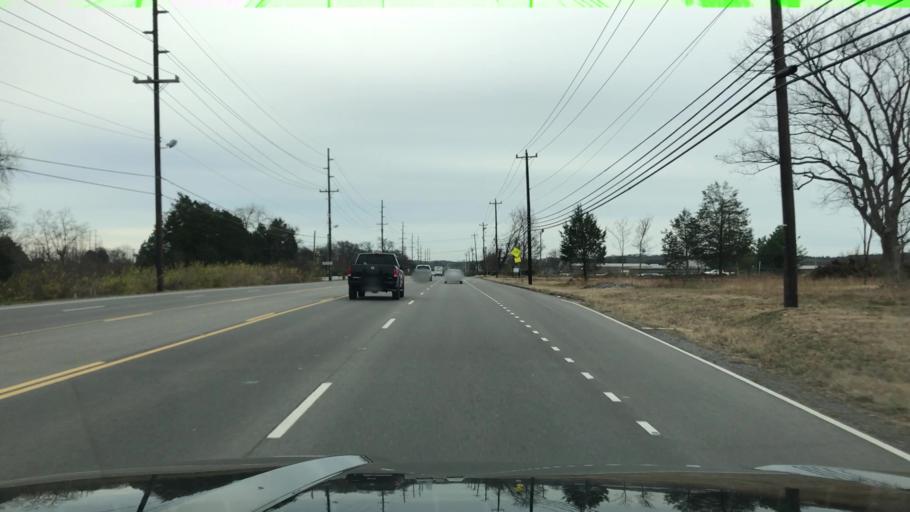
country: US
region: Tennessee
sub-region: Rutherford County
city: La Vergne
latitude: 36.0331
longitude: -86.5959
